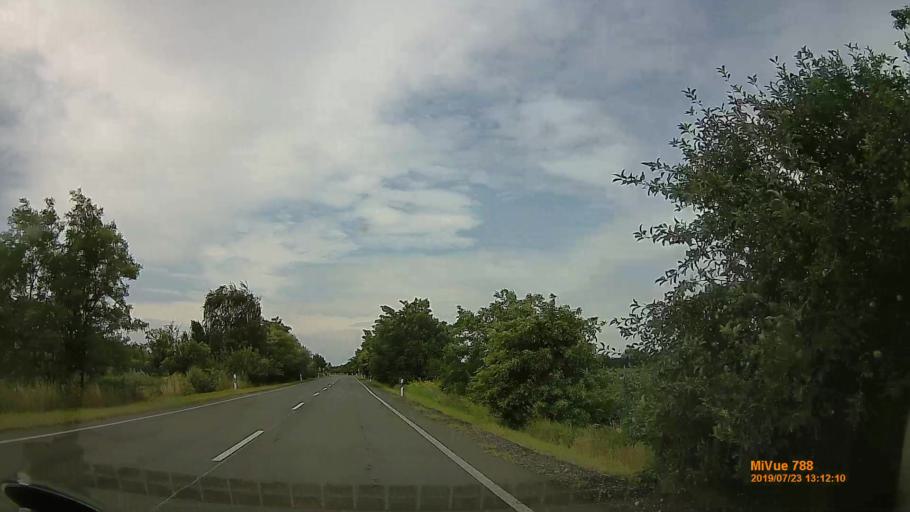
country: HU
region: Hajdu-Bihar
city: Gorbehaza
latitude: 47.9301
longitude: 21.2567
